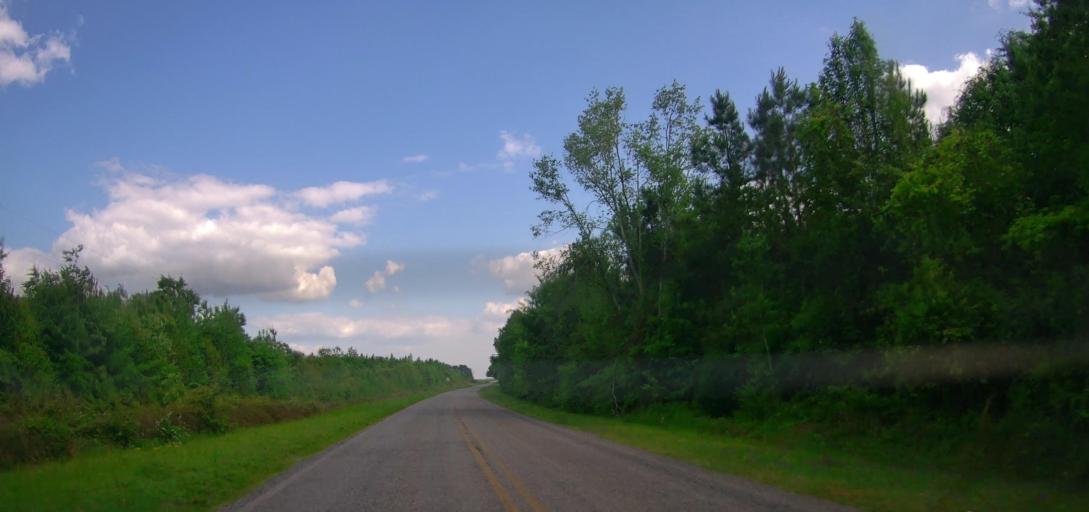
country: US
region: Georgia
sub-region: Laurens County
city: East Dublin
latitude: 32.6919
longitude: -82.9015
